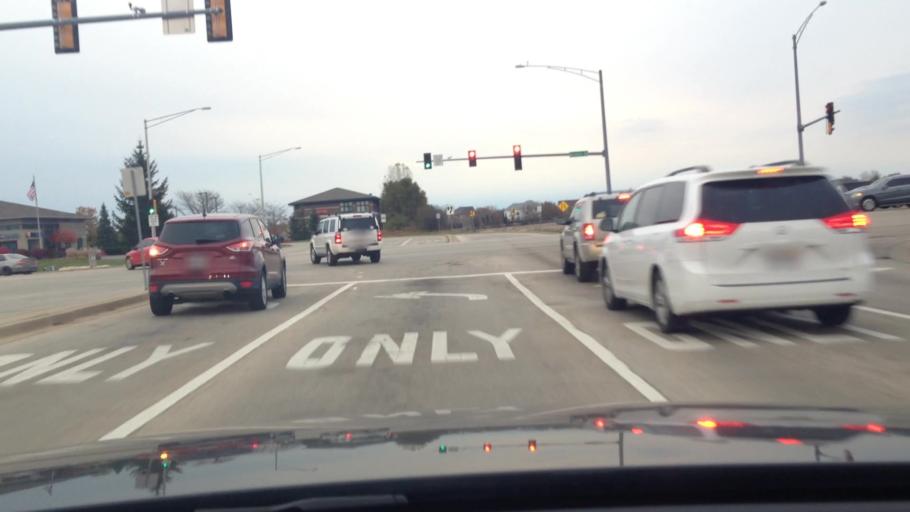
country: US
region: Illinois
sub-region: McHenry County
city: Lake in the Hills
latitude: 42.1612
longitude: -88.3362
